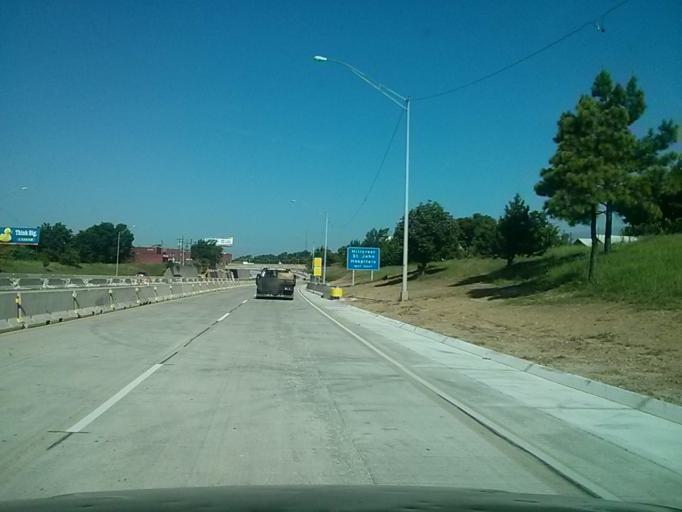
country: US
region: Oklahoma
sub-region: Tulsa County
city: Tulsa
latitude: 36.1606
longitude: -95.9547
